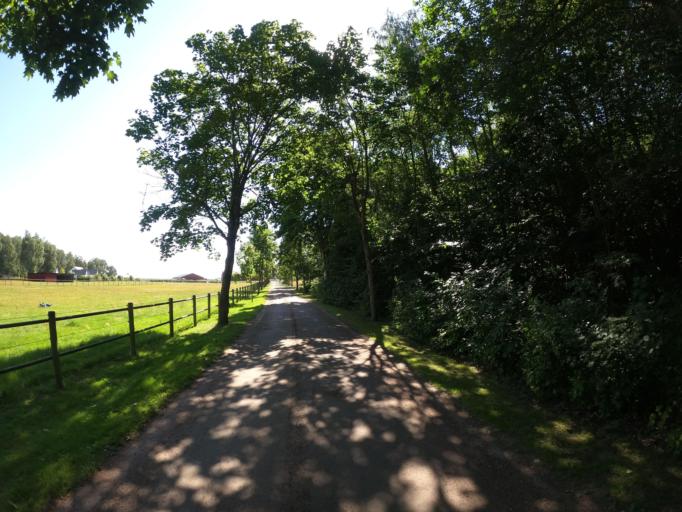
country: SE
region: Skane
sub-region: Lunds Kommun
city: Genarp
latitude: 55.6722
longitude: 13.4106
